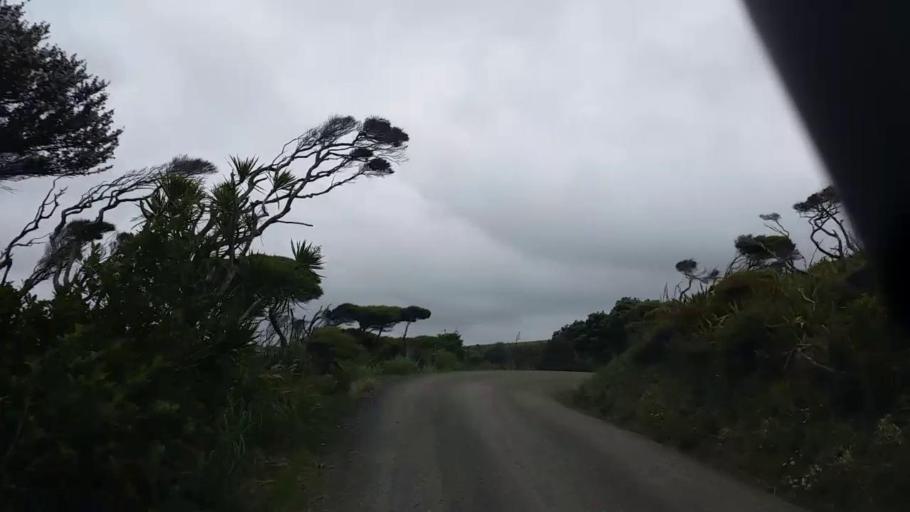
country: NZ
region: Auckland
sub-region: Auckland
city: Muriwai Beach
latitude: -36.9317
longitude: 174.4648
